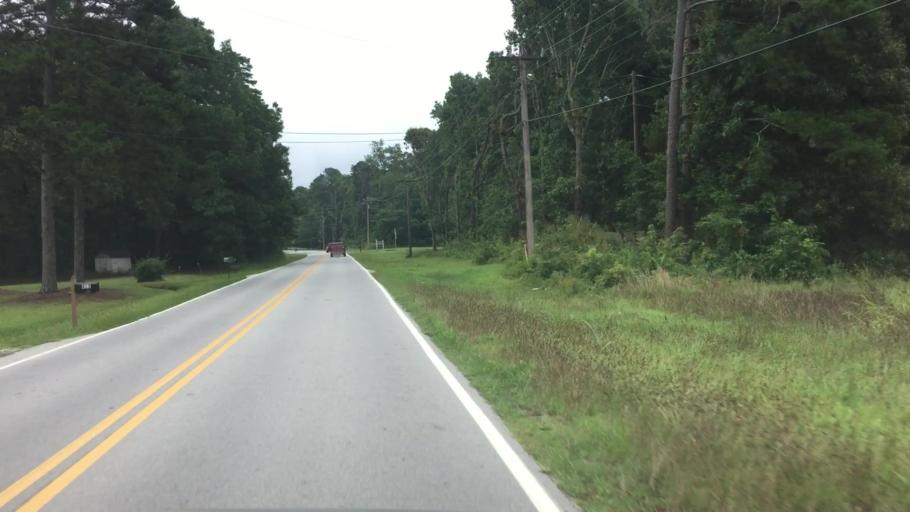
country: US
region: Georgia
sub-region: Barrow County
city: Winder
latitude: 34.0261
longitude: -83.7465
